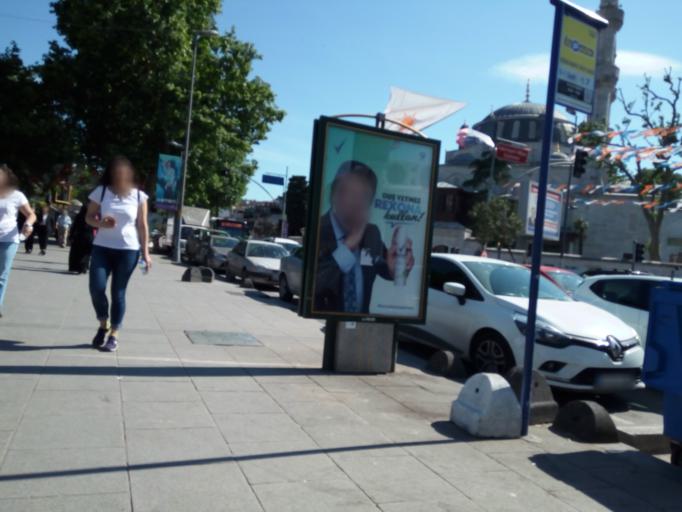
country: TR
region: Istanbul
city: UEskuedar
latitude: 41.0254
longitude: 29.0158
